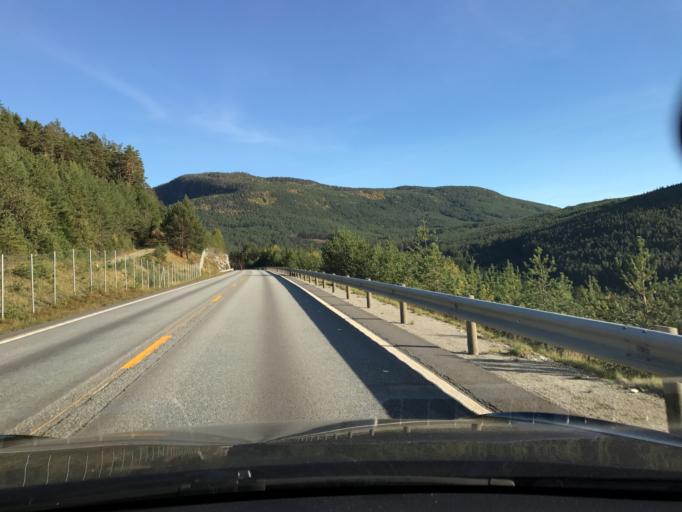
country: NO
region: Sogn og Fjordane
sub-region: Sogndal
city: Sogndalsfjora
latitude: 61.1822
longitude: 7.2731
